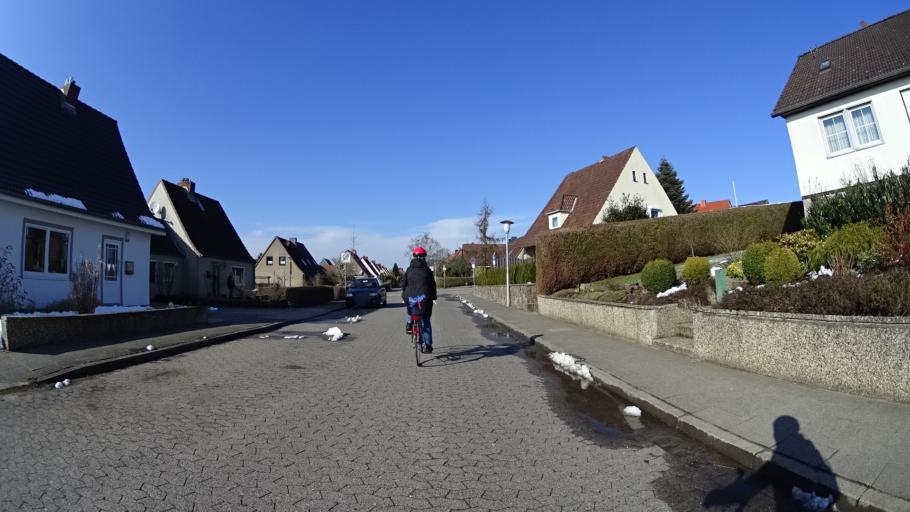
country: DE
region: Schleswig-Holstein
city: Schellhorn
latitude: 54.2402
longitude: 10.2913
